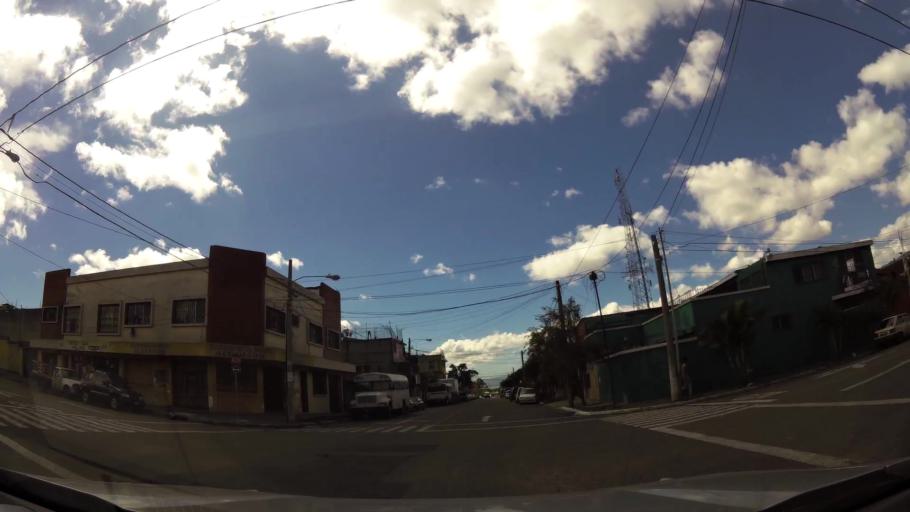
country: GT
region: Guatemala
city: Guatemala City
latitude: 14.6030
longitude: -90.5462
